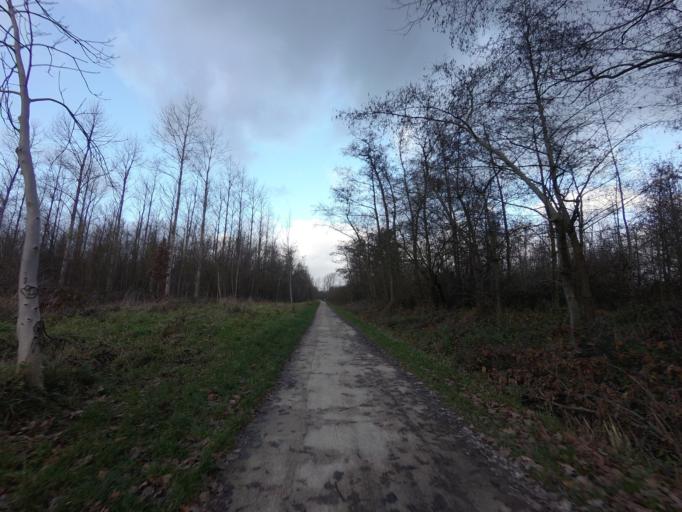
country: BE
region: Flanders
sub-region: Provincie Vlaams-Brabant
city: Haacht
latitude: 50.9637
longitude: 4.6317
